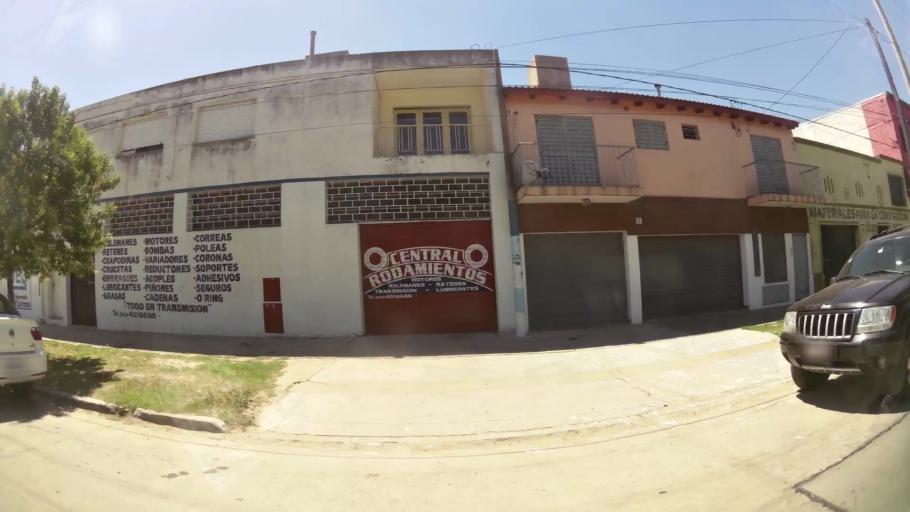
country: AR
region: Cordoba
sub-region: Departamento de Capital
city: Cordoba
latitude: -31.3939
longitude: -64.1541
